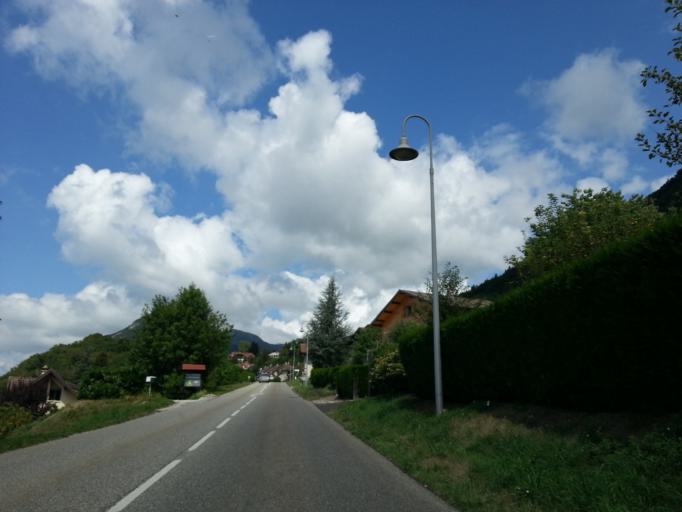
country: FR
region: Rhone-Alpes
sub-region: Departement de la Haute-Savoie
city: Talloires
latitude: 45.8488
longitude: 6.2165
